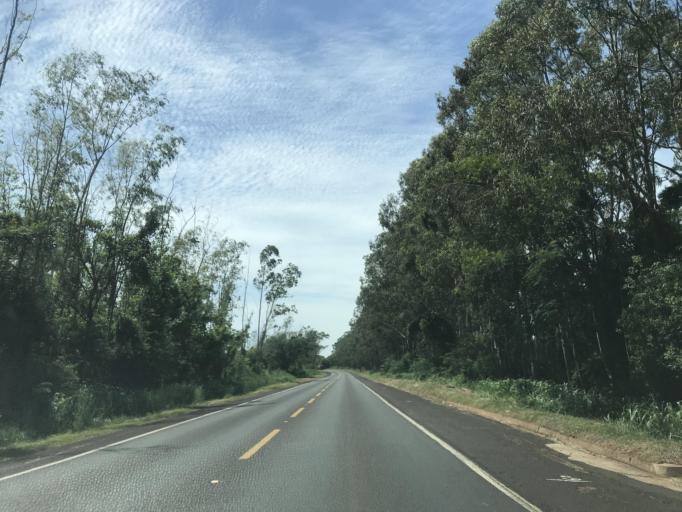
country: BR
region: Parana
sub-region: Paranavai
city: Nova Aurora
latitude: -22.9575
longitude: -52.6935
